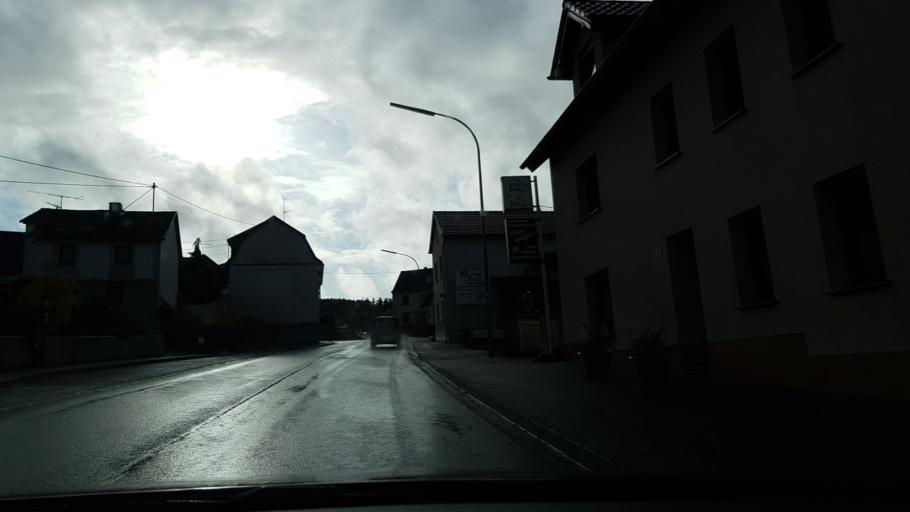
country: DE
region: Rheinland-Pfalz
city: Quiddelbach
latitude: 50.3518
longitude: 6.9384
